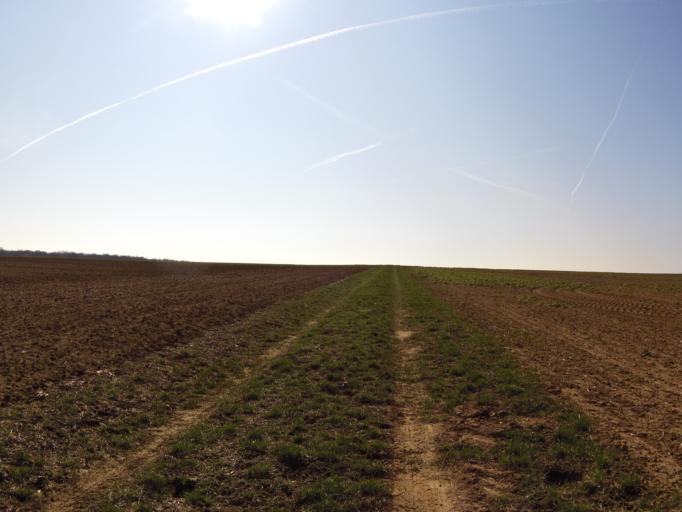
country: DE
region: Bavaria
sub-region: Regierungsbezirk Unterfranken
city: Rottendorf
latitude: 49.8172
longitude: 10.0265
